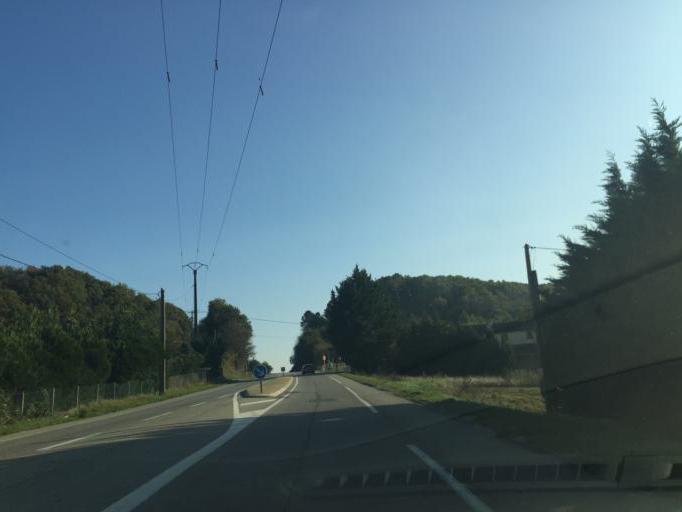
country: FR
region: Rhone-Alpes
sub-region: Departement de la Drome
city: Peyrins
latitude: 45.1116
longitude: 5.0038
